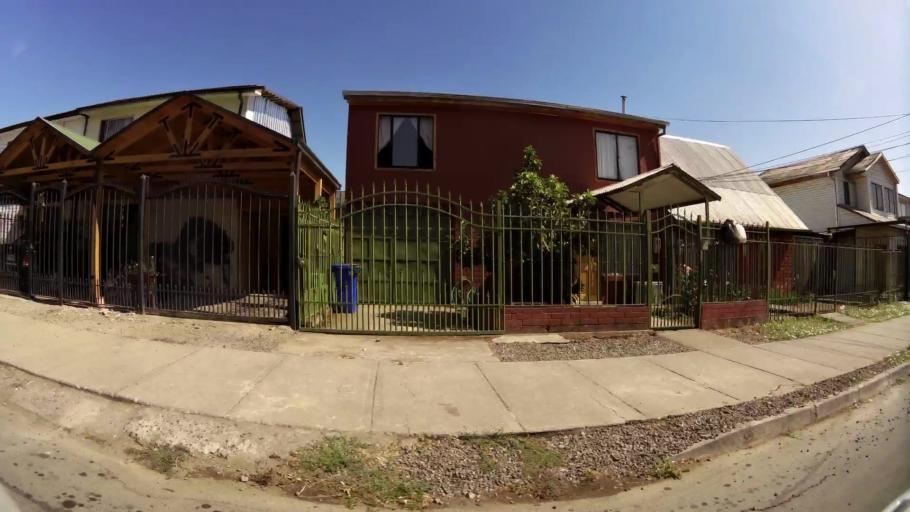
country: CL
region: Maule
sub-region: Provincia de Talca
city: Talca
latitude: -35.4120
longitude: -71.6388
